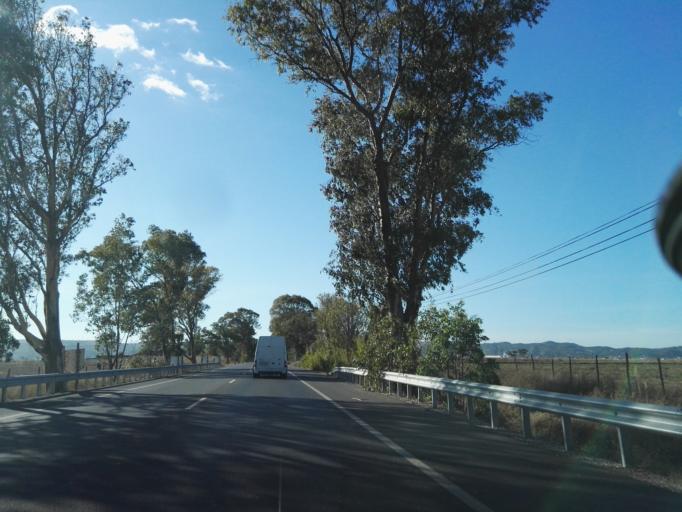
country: PT
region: Lisbon
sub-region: Vila Franca de Xira
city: Vila Franca de Xira
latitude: 38.9403
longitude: -8.9395
